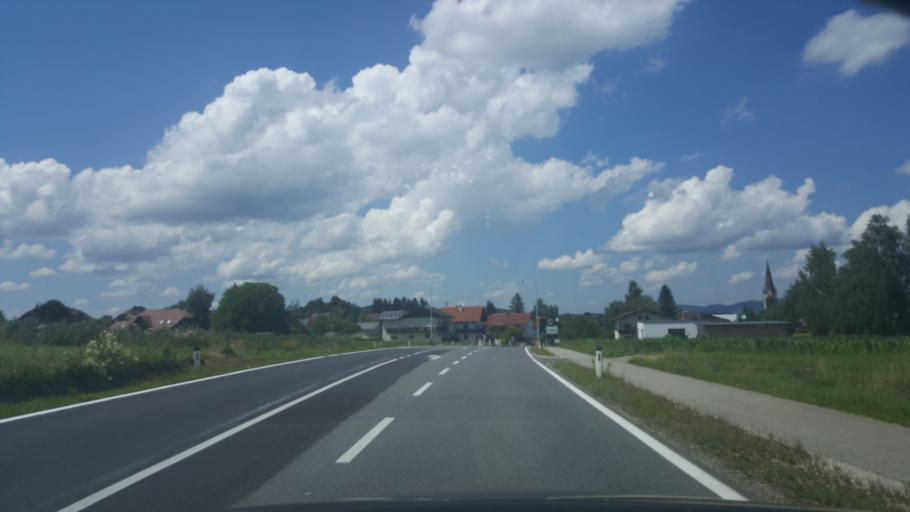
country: AT
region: Upper Austria
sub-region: Politischer Bezirk Vocklabruck
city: Gampern
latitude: 47.9839
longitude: 13.5564
